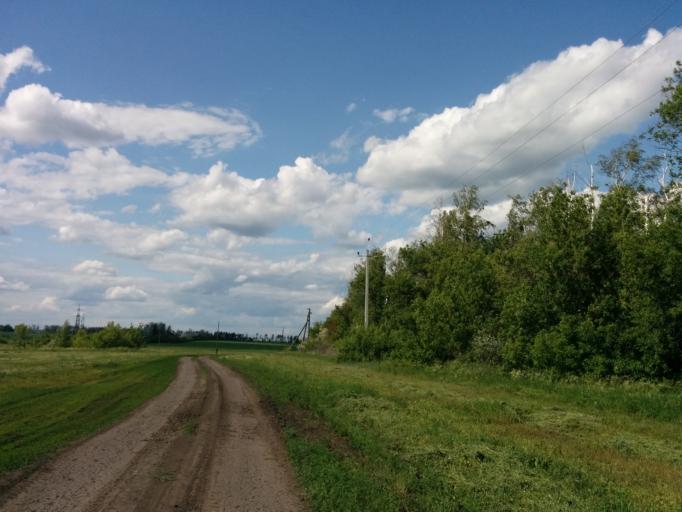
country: RU
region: Tambov
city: Tambov
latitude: 52.7923
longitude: 41.3832
